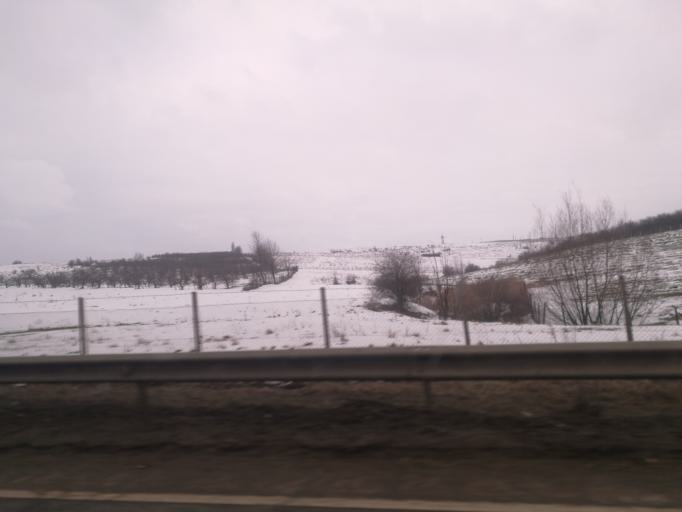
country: RO
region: Suceava
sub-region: Municipiul Falticeni
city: Falticeni
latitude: 47.4459
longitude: 26.2940
